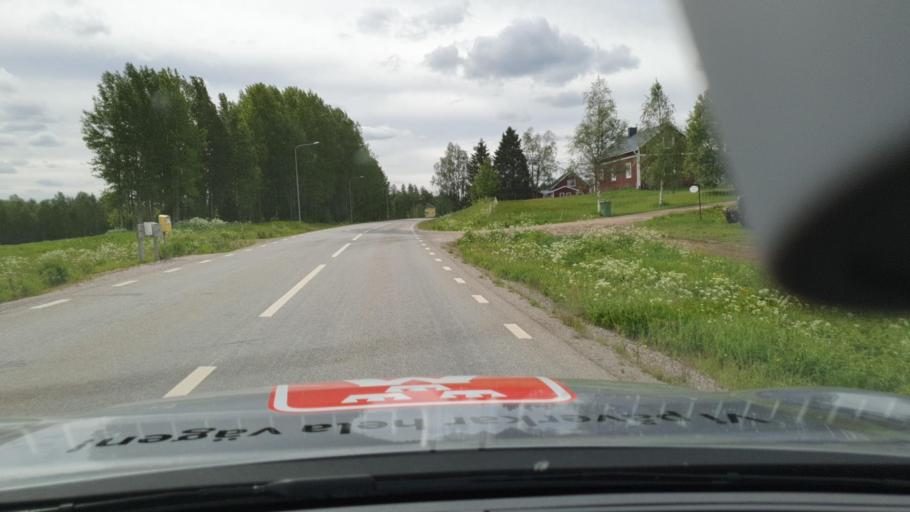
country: SE
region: Norrbotten
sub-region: Kalix Kommun
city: Kalix
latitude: 65.9705
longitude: 23.4608
